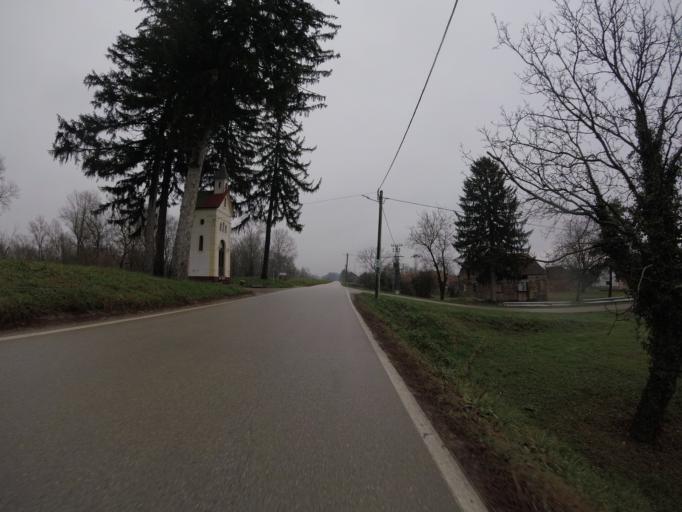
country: HR
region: Zagrebacka
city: Kuce
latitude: 45.6959
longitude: 16.2203
